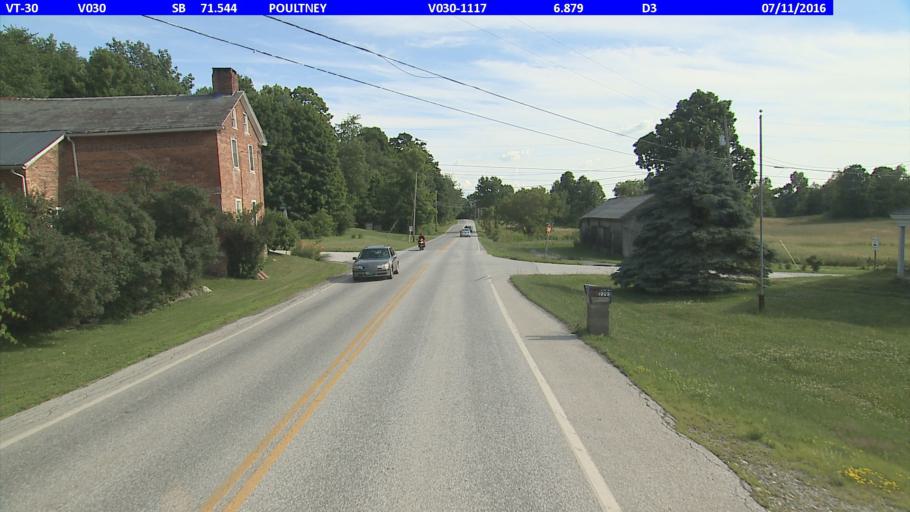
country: US
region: Vermont
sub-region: Rutland County
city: Poultney
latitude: 43.5501
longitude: -73.2266
